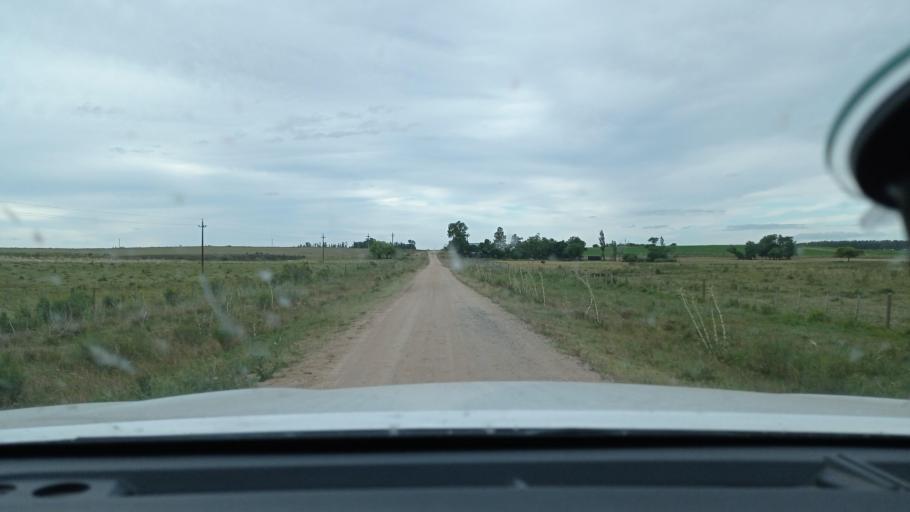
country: UY
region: Florida
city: Casupa
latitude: -34.1212
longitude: -55.7713
